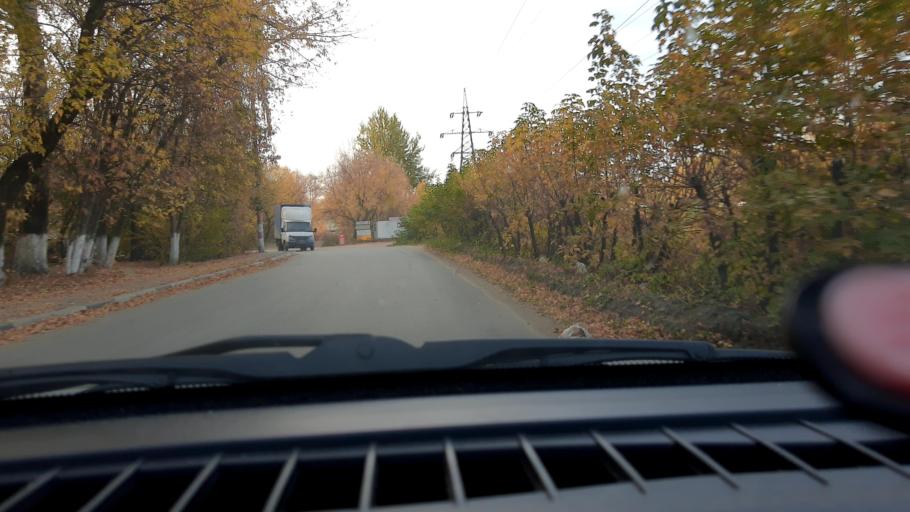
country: RU
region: Nizjnij Novgorod
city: Nizhniy Novgorod
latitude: 56.3111
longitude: 43.8804
